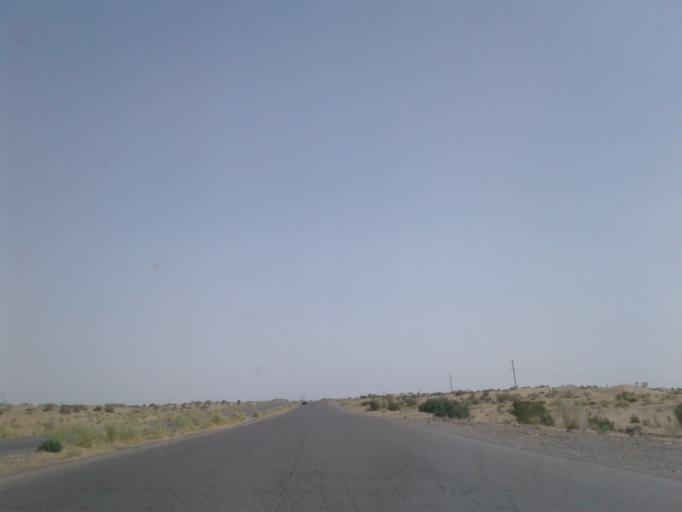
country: TM
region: Ahal
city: Abadan
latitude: 38.9014
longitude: 58.5009
